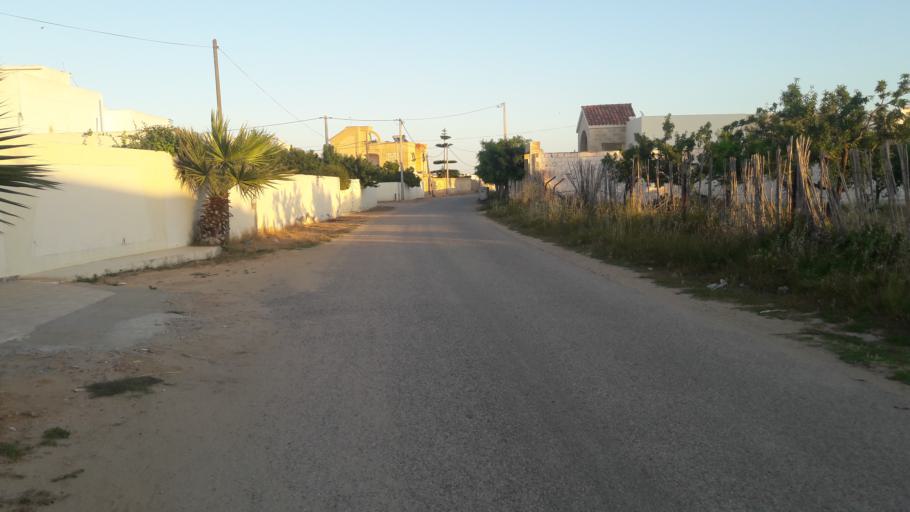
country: TN
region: Safaqis
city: Sfax
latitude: 34.8102
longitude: 10.7432
